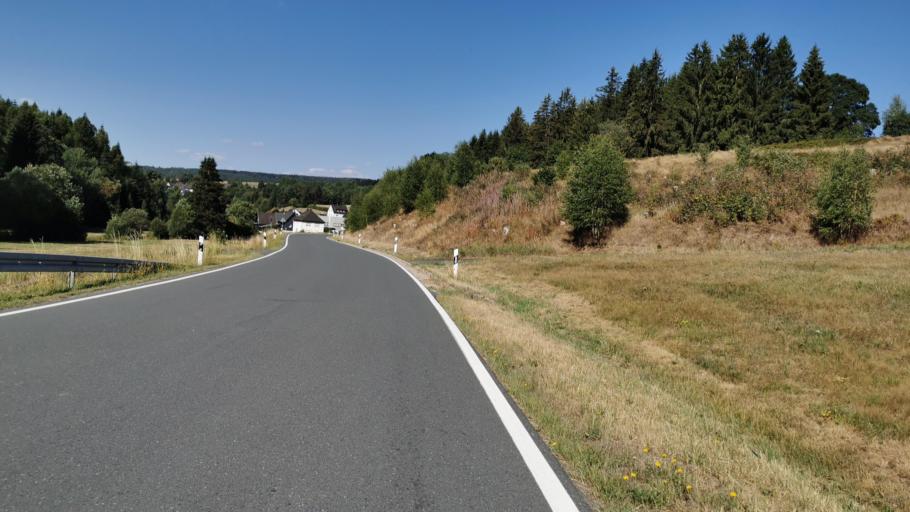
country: DE
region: Bavaria
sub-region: Upper Franconia
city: Tettau
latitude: 50.4359
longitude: 11.2973
